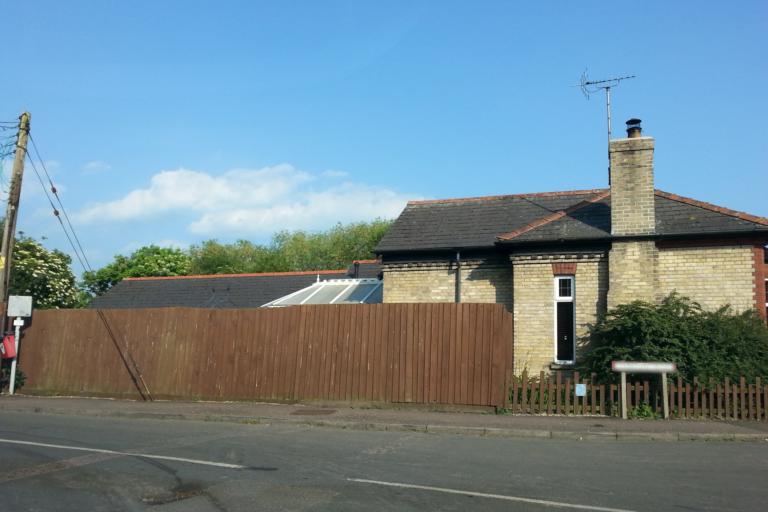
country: GB
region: England
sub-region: Cambridgeshire
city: Swavesey
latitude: 52.3179
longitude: 0.0134
